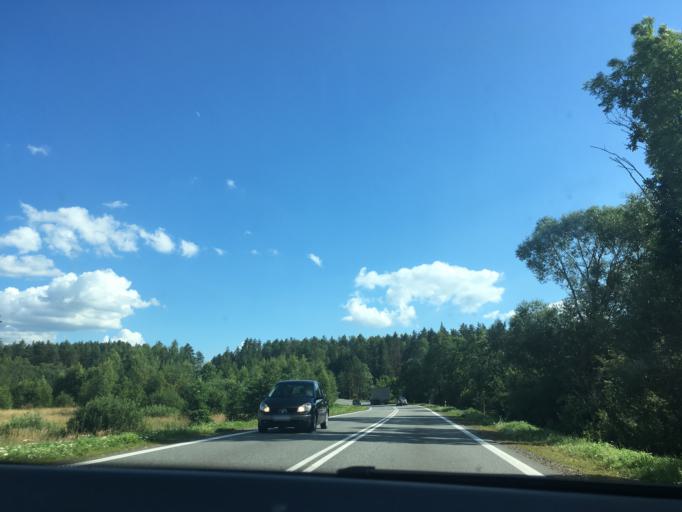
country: PL
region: Podlasie
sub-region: Powiat bialostocki
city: Wasilkow
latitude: 53.2724
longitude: 23.1200
